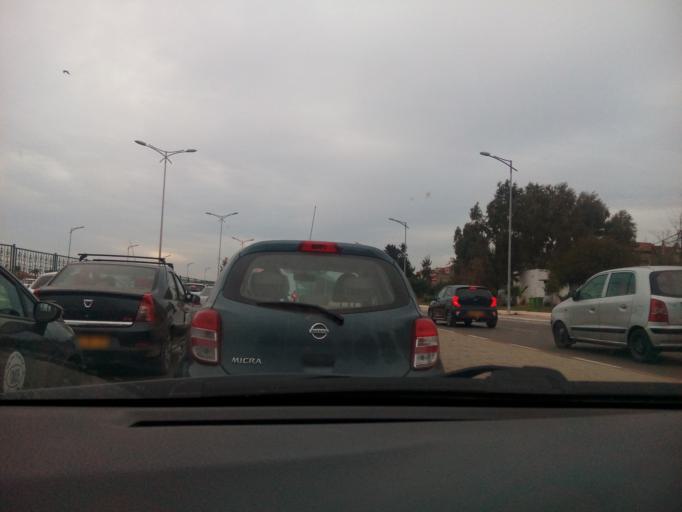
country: DZ
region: Oran
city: Oran
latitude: 35.6796
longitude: -0.6144
